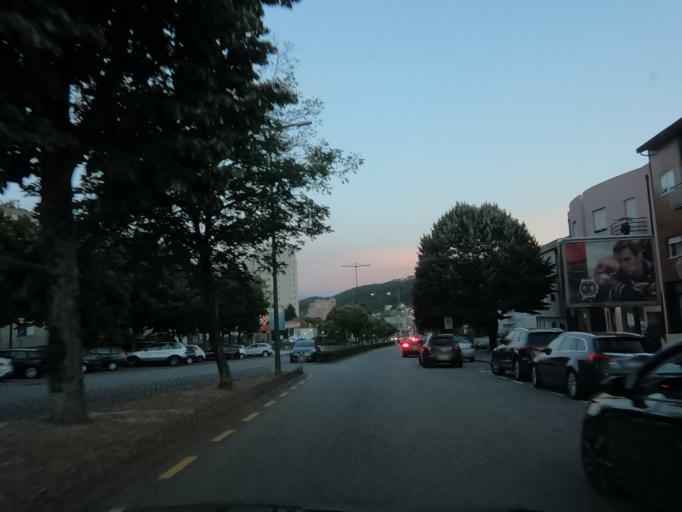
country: PT
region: Porto
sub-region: Valongo
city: Valongo
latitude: 41.1930
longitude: -8.4995
